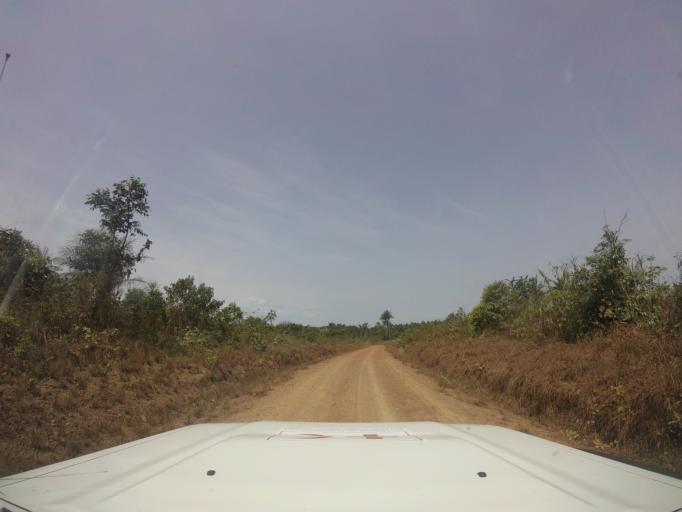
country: LR
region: Grand Cape Mount
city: Robertsport
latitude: 6.9333
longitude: -11.3447
